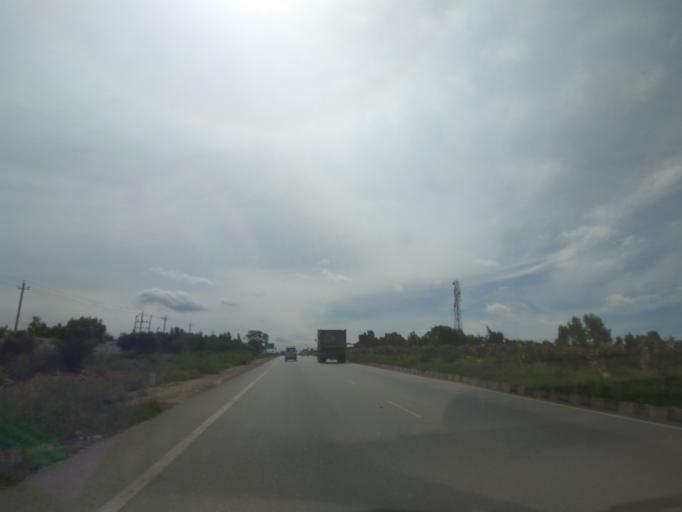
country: IN
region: Karnataka
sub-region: Bangalore Rural
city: Dasarahalli
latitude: 13.1318
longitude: 77.9545
